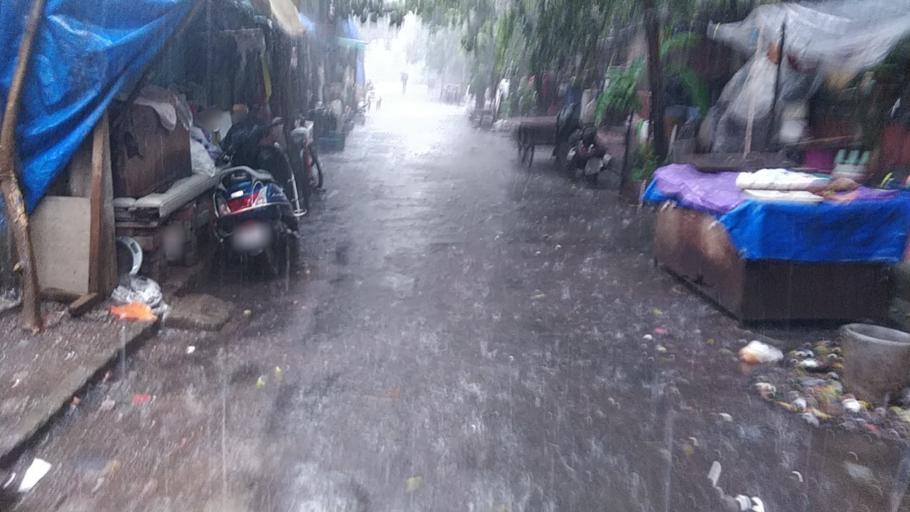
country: IN
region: Maharashtra
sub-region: Mumbai Suburban
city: Mumbai
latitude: 19.0790
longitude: 72.8321
